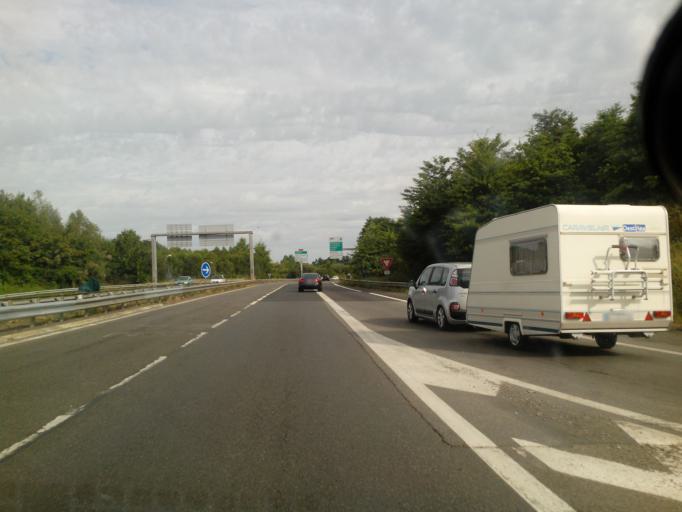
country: FR
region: Pays de la Loire
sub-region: Departement de la Loire-Atlantique
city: Orvault
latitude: 47.2645
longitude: -1.5855
